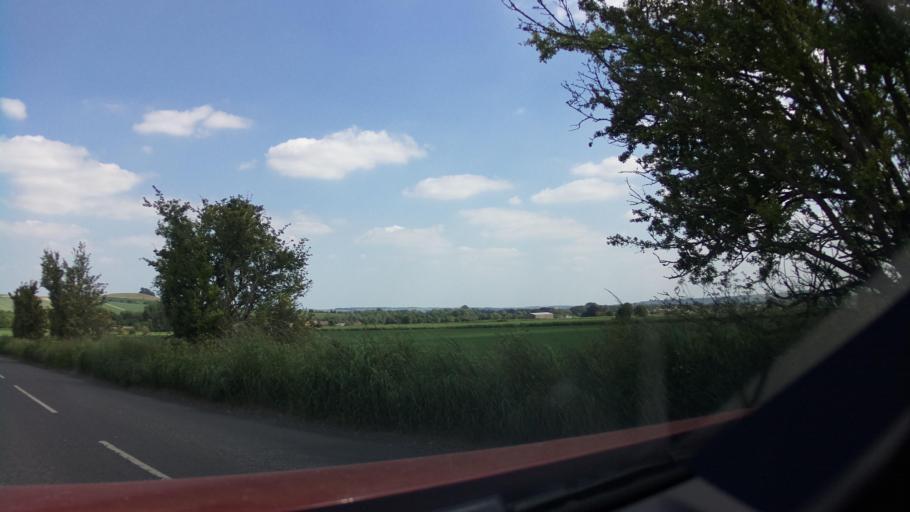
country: GB
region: England
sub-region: Wiltshire
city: Woodborough
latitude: 51.3612
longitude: -1.8574
